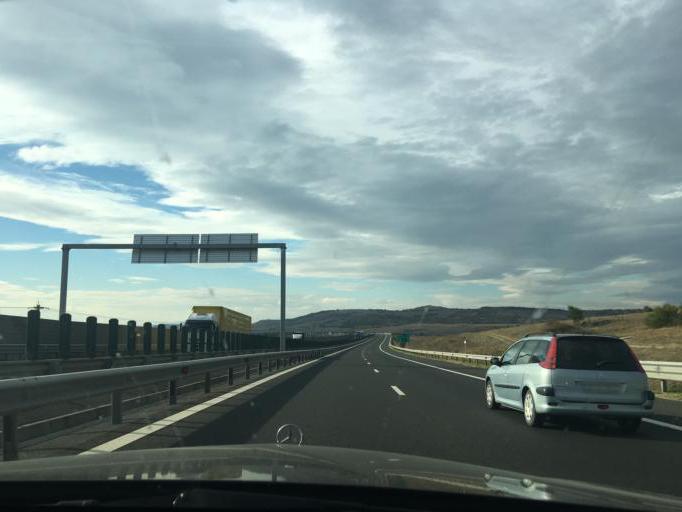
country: RO
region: Sibiu
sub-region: Comuna Apoldu de Jos
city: Apoldu de Jos
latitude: 45.8801
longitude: 23.8594
